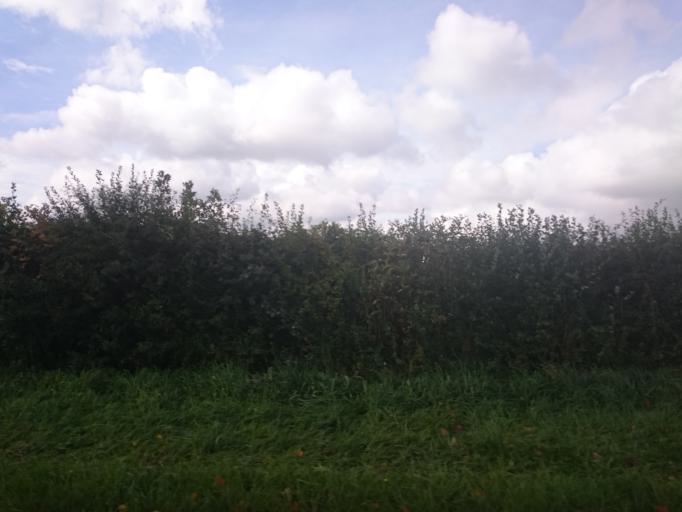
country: GB
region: England
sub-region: Gloucestershire
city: Charlton Kings
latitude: 51.7988
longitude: -2.0495
